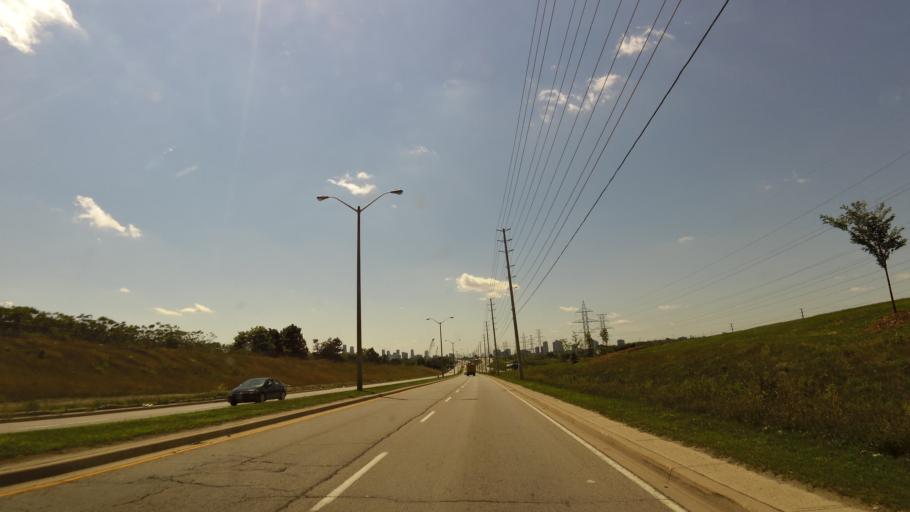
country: CA
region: Ontario
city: Etobicoke
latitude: 43.6274
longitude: -79.6174
